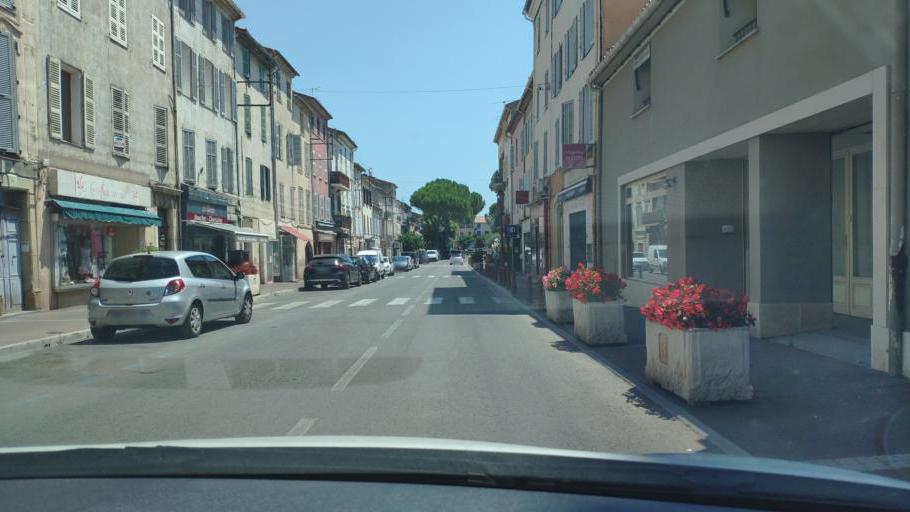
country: FR
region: Provence-Alpes-Cote d'Azur
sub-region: Departement du Var
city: Les Arcs
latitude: 43.4623
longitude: 6.4789
